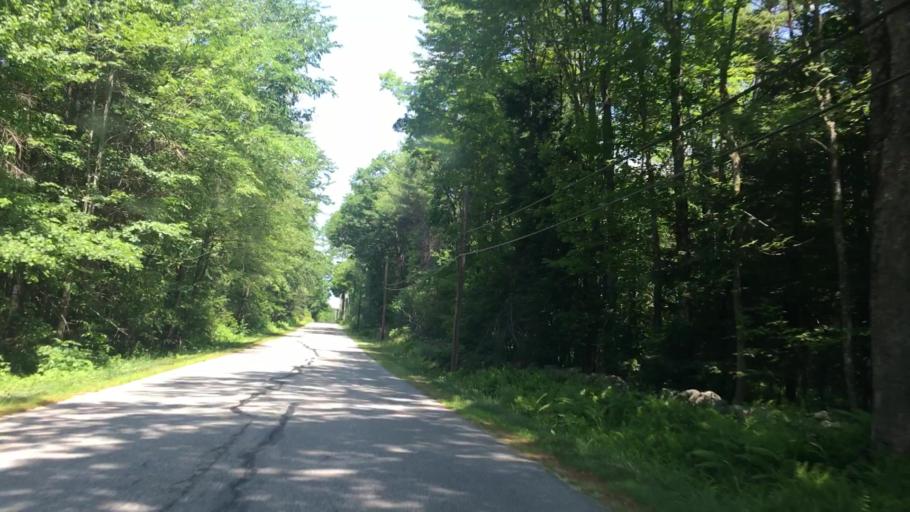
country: US
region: Maine
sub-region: Kennebec County
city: Wayne
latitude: 44.3340
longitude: -70.0577
